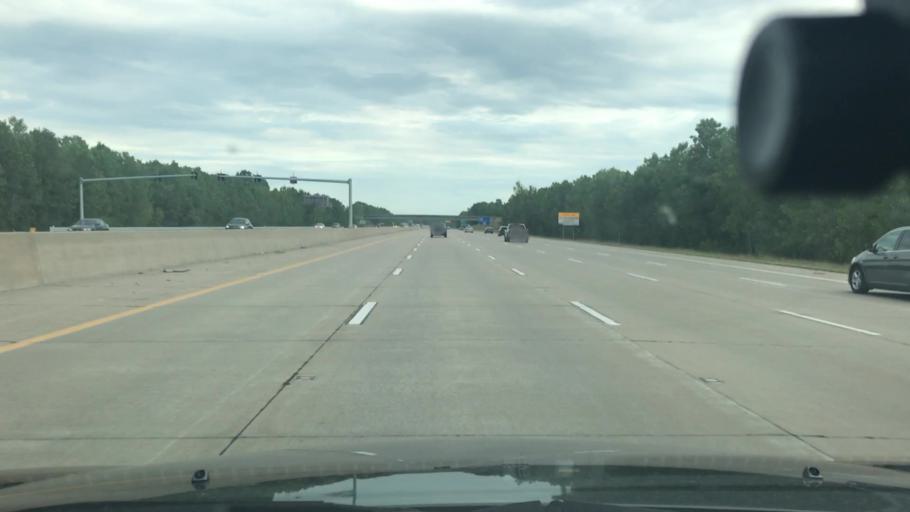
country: US
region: Missouri
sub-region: Saint Charles County
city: Saint Charles
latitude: 38.7237
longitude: -90.5130
